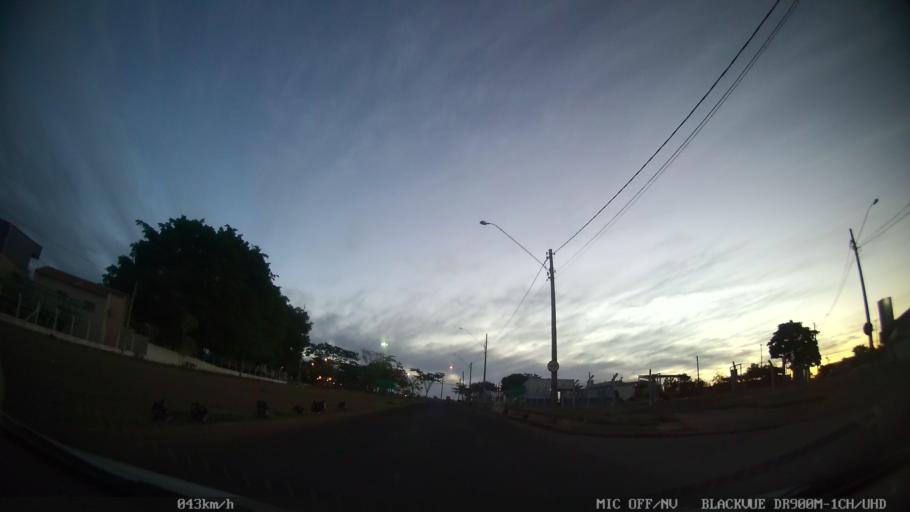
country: BR
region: Sao Paulo
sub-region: Catanduva
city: Catanduva
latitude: -21.1505
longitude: -48.9969
